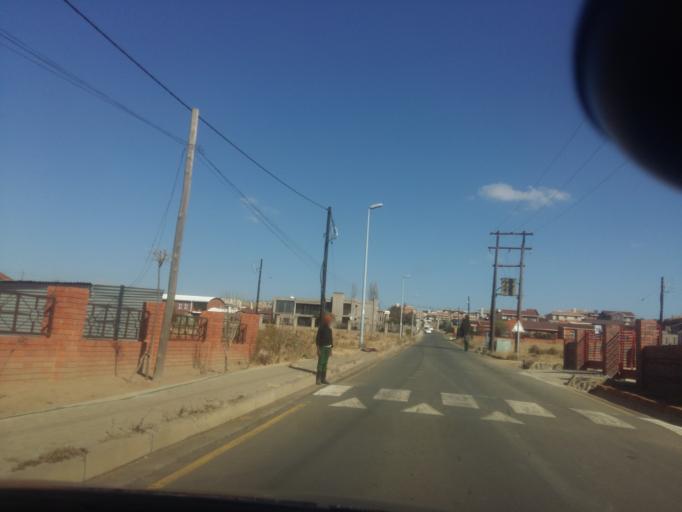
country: LS
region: Maseru
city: Maseru
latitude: -29.3447
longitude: 27.4501
